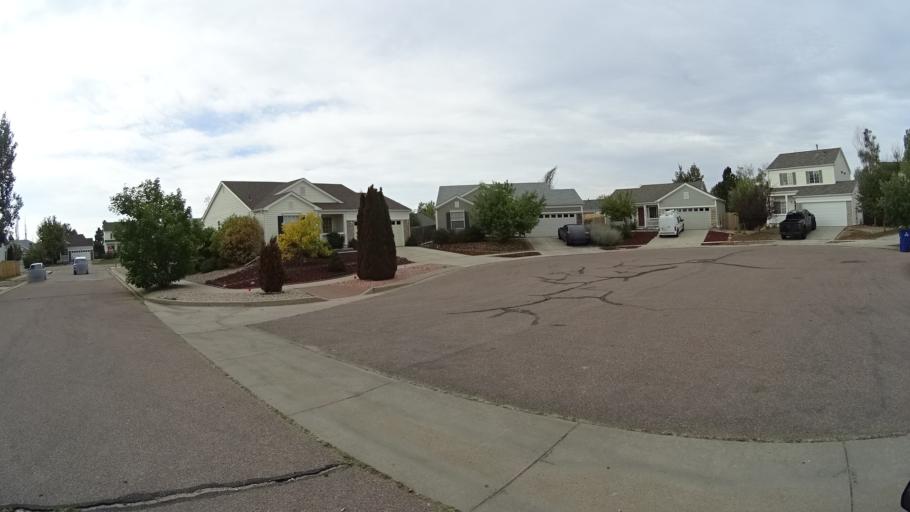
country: US
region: Colorado
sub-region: El Paso County
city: Cimarron Hills
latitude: 38.9121
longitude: -104.7084
